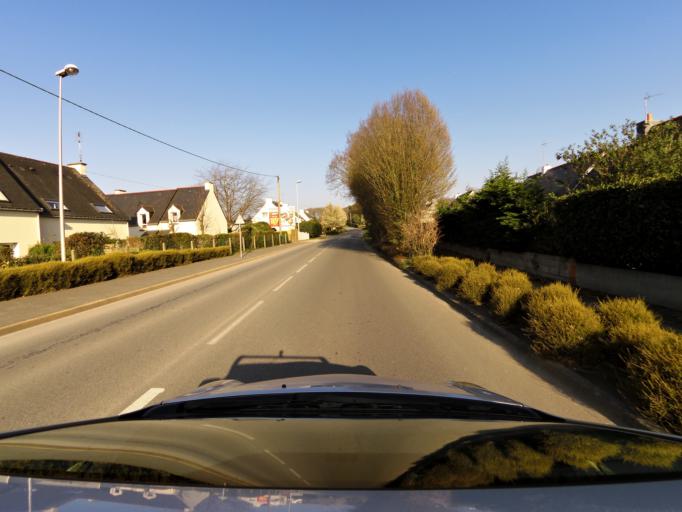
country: FR
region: Brittany
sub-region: Departement du Morbihan
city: Ploemeur
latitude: 47.7370
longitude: -3.4372
